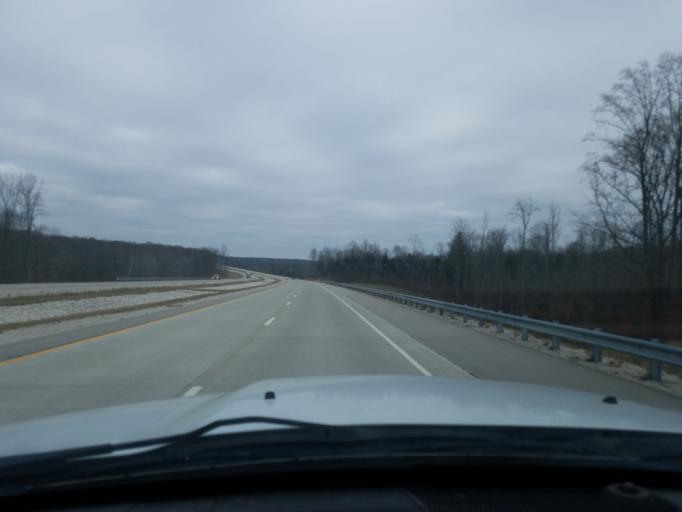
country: US
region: Indiana
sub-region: Monroe County
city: Bloomington
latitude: 39.0709
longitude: -86.6157
